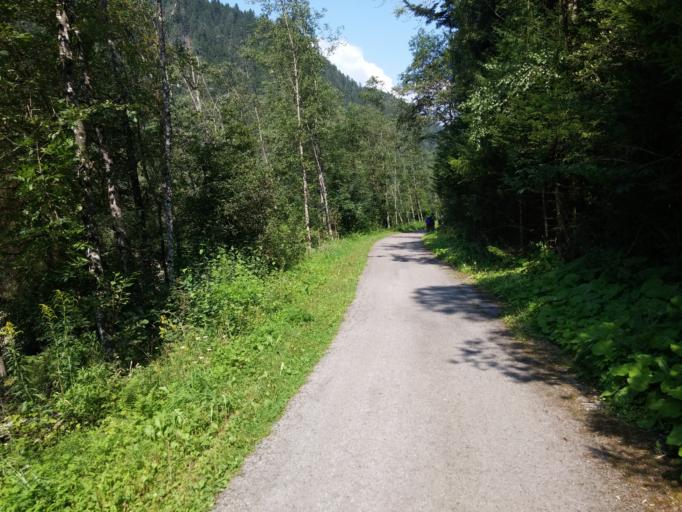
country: AT
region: Tyrol
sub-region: Politischer Bezirk Lienz
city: Leisach
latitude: 46.7885
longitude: 12.7032
